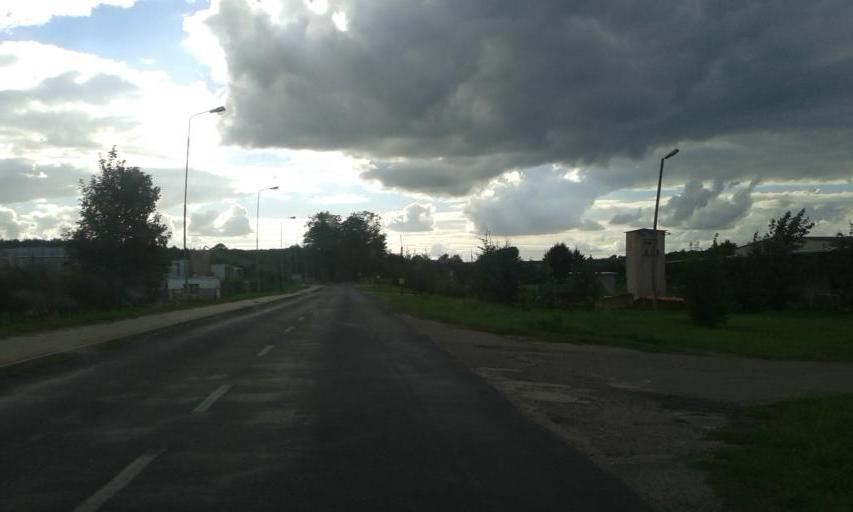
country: PL
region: West Pomeranian Voivodeship
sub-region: Powiat szczecinecki
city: Barwice
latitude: 53.7450
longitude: 16.3462
